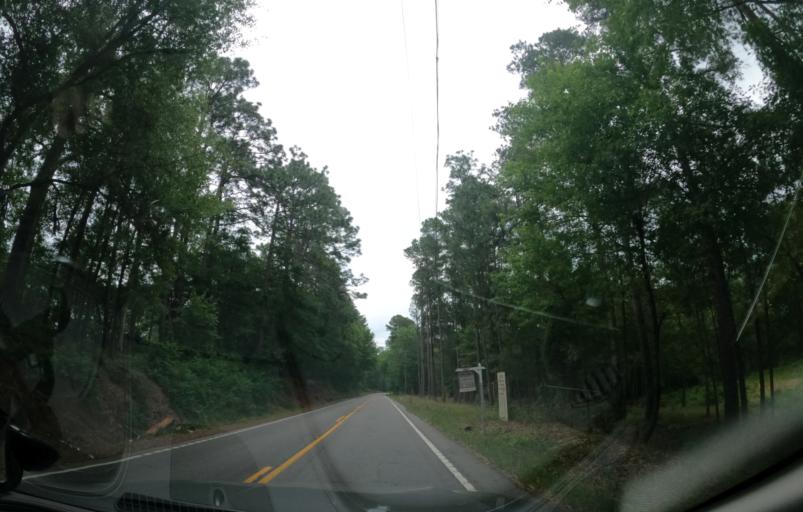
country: US
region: South Carolina
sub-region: Aiken County
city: Aiken
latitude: 33.5738
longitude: -81.6849
